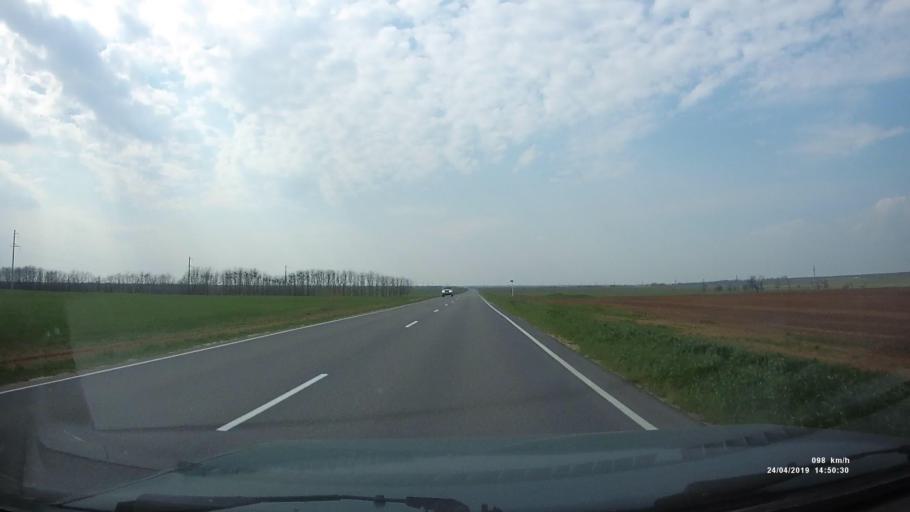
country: RU
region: Rostov
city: Remontnoye
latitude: 46.5178
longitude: 43.7182
